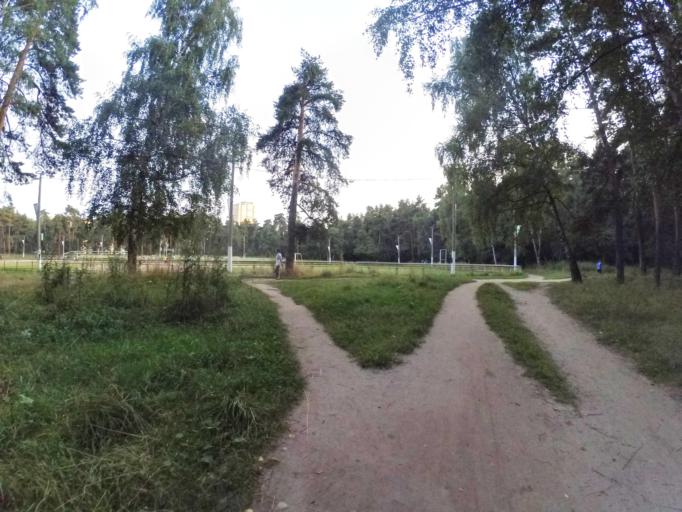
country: RU
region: Moskovskaya
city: Kotel'niki
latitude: 55.6658
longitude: 37.8472
